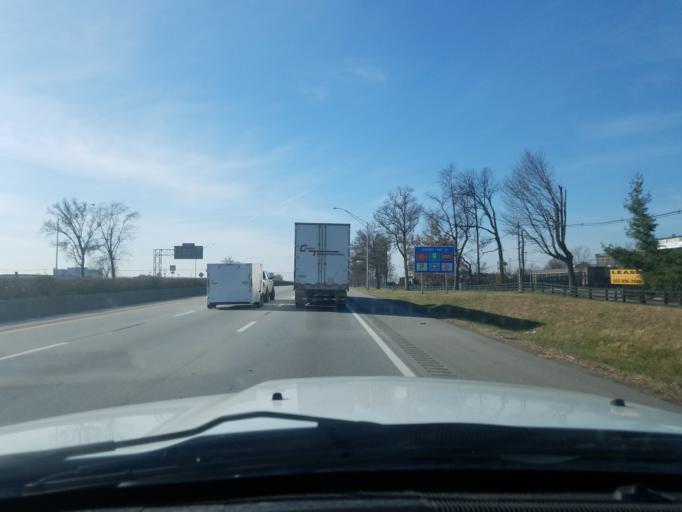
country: US
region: Kentucky
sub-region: Jefferson County
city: Douglass Hills
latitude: 38.2231
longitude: -85.5641
